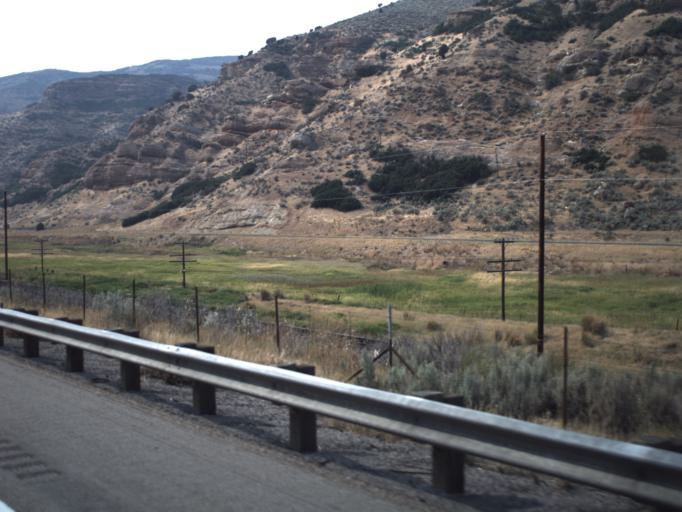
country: US
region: Utah
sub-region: Summit County
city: Coalville
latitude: 41.0259
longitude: -111.3490
